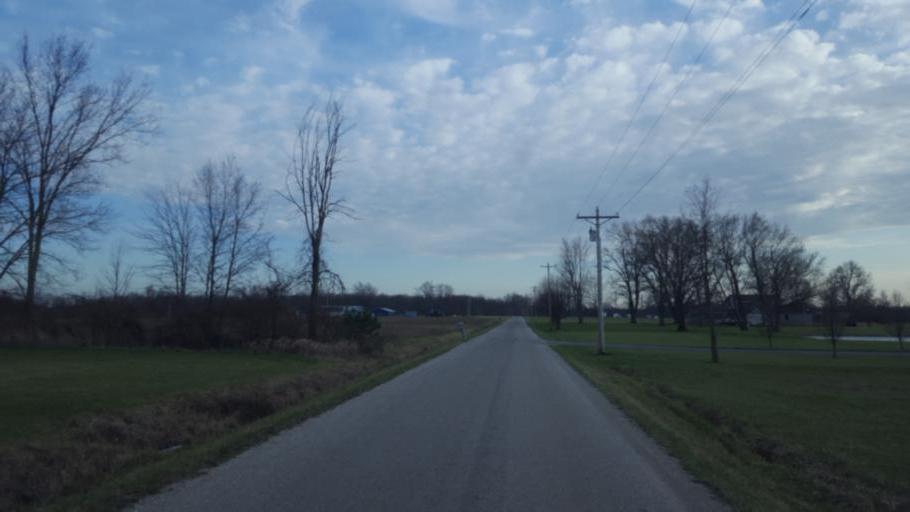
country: US
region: Ohio
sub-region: Crawford County
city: Bucyrus
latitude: 40.6694
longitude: -82.9484
